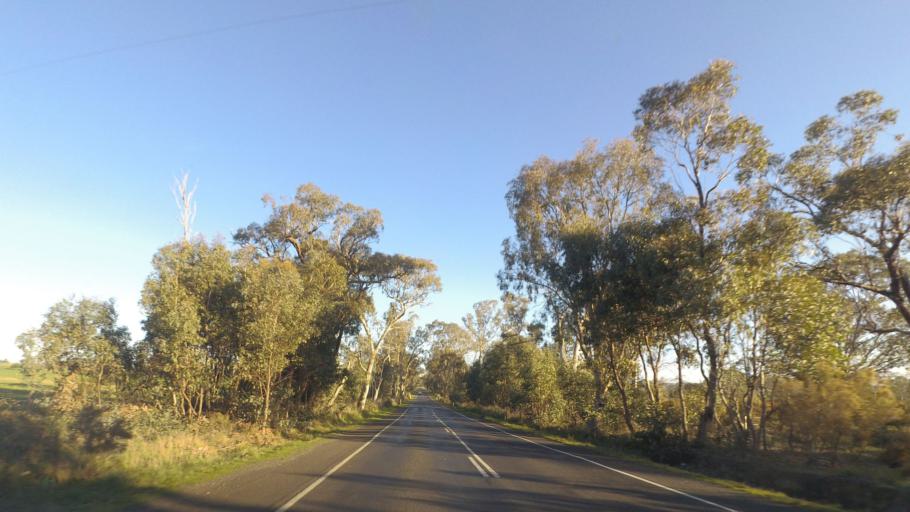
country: AU
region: Victoria
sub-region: Mount Alexander
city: Castlemaine
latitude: -37.0798
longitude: 144.5078
